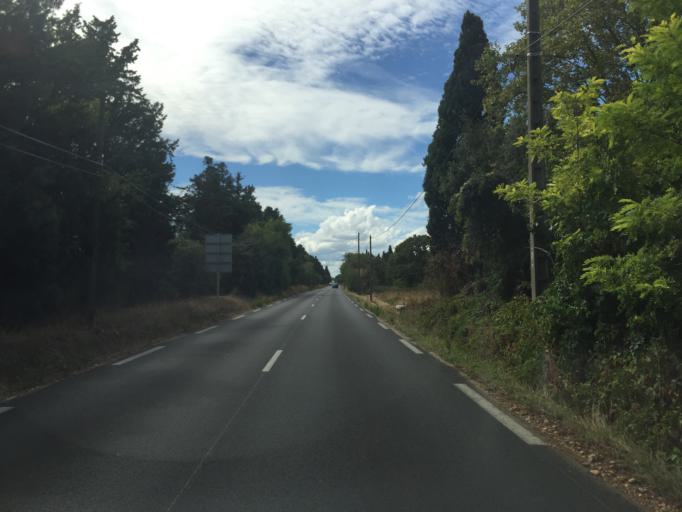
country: FR
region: Provence-Alpes-Cote d'Azur
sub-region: Departement du Vaucluse
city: Orange
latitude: 44.1181
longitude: 4.7969
